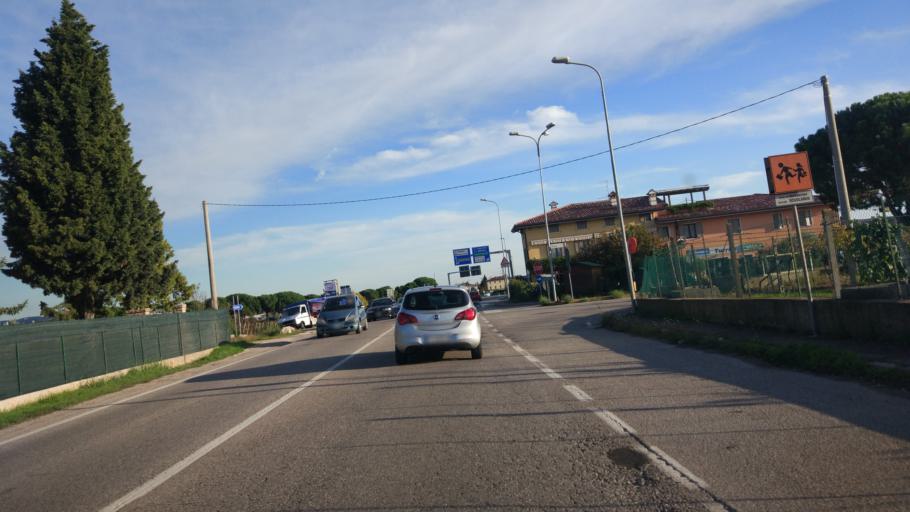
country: IT
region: Veneto
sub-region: Provincia di Verona
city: Pescantina
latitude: 45.5002
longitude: 10.8598
